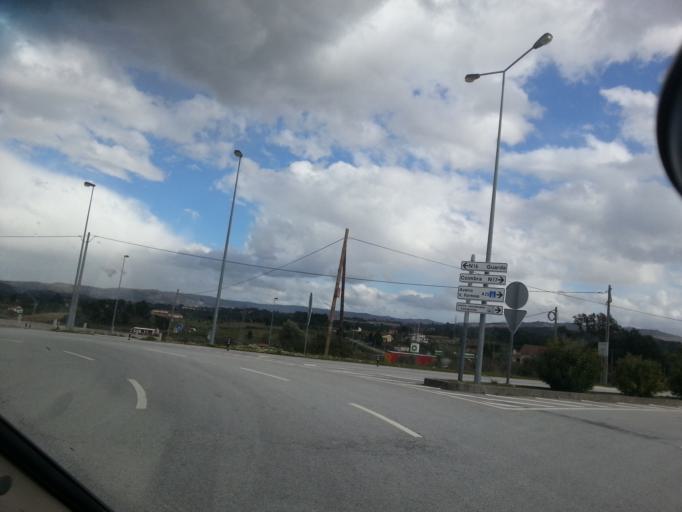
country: PT
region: Guarda
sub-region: Celorico da Beira
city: Celorico da Beira
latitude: 40.6429
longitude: -7.3844
